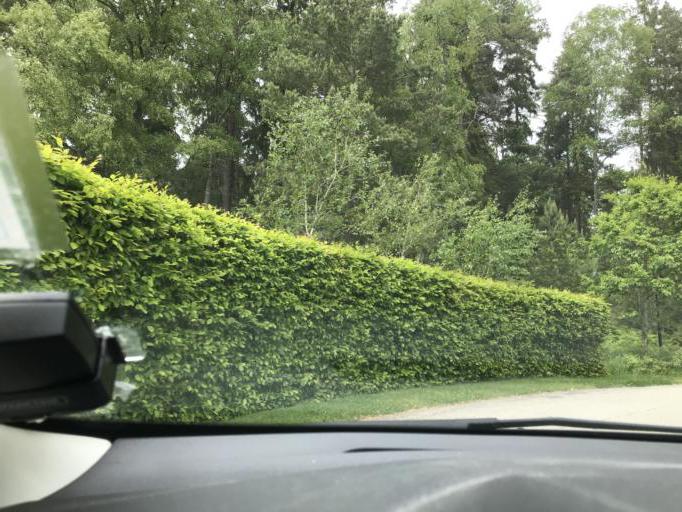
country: SE
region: Stockholm
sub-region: Botkyrka Kommun
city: Alby
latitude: 59.2192
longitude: 17.8495
